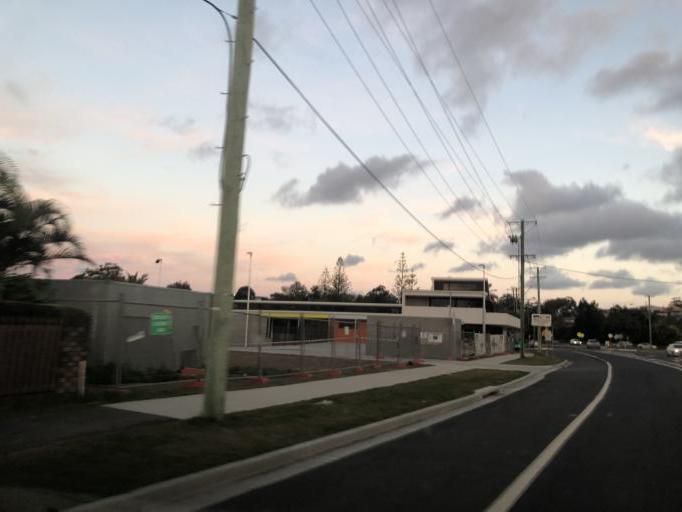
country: AU
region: New South Wales
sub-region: Coffs Harbour
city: Woolgoolga
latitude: -30.1114
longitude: 153.1903
